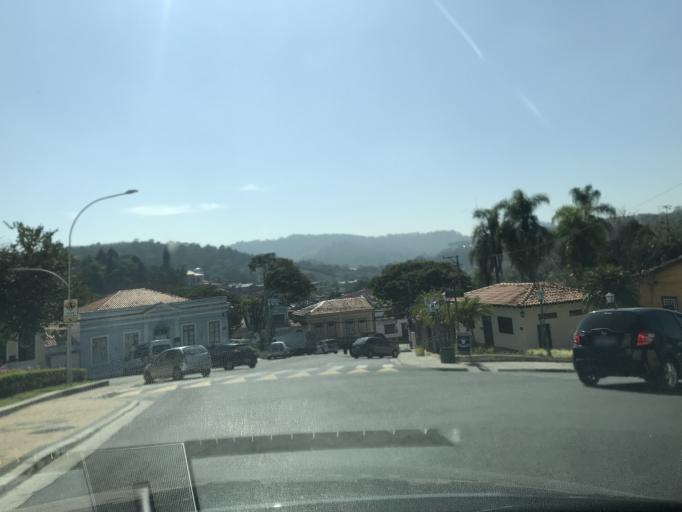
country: BR
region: Sao Paulo
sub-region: Santana De Parnaiba
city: Santana de Parnaiba
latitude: -23.4457
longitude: -46.9139
